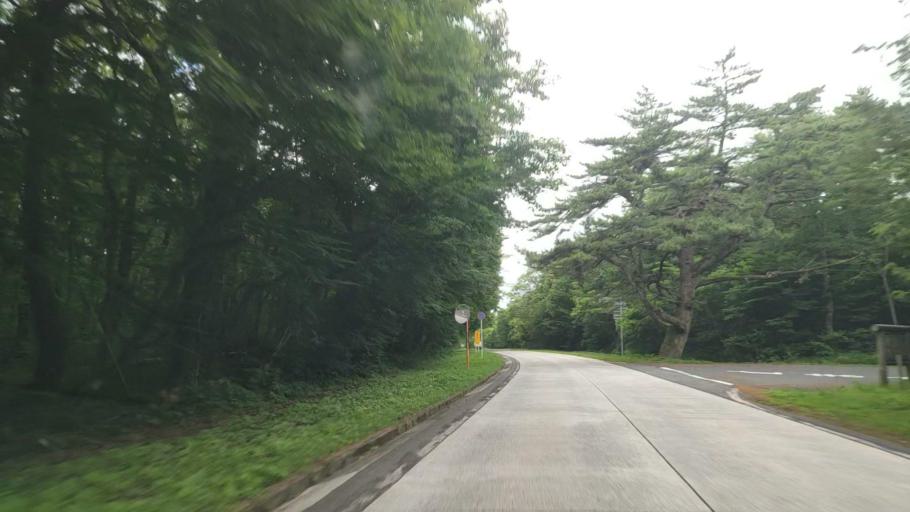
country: JP
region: Tottori
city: Yonago
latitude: 35.3983
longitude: 133.5091
